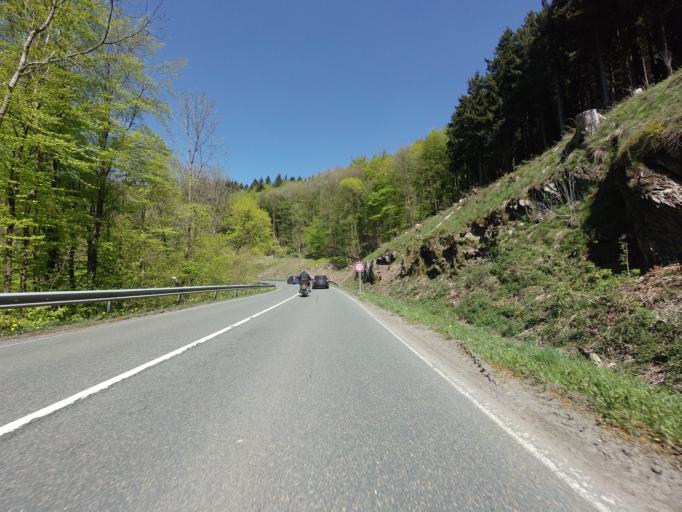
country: DE
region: North Rhine-Westphalia
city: Hilchenbach
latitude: 50.9700
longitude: 8.1573
